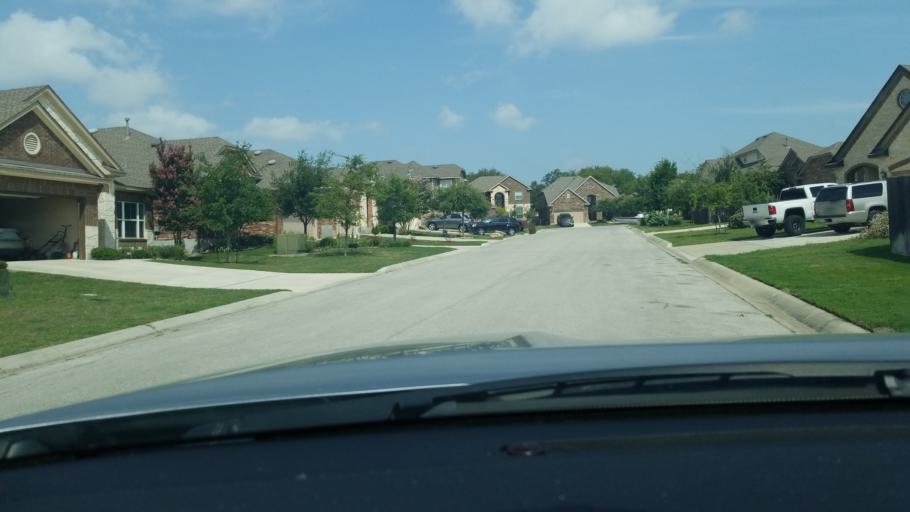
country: US
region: Texas
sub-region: Bexar County
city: Timberwood Park
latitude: 29.6910
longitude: -98.4924
